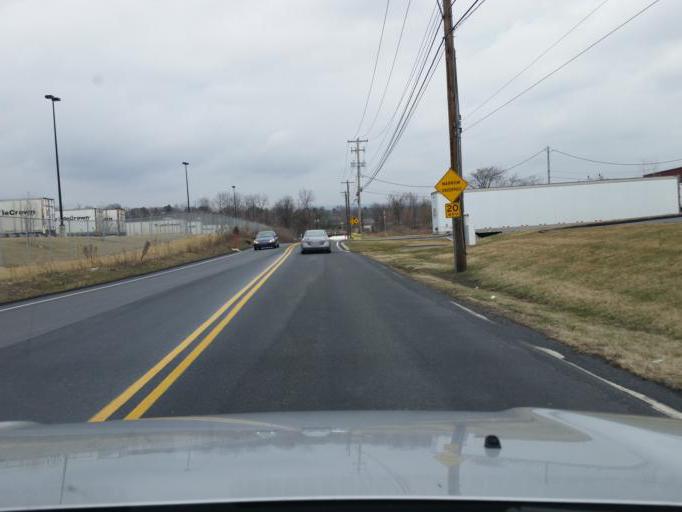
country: US
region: Pennsylvania
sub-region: Dauphin County
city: Rutherford
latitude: 40.2649
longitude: -76.7473
